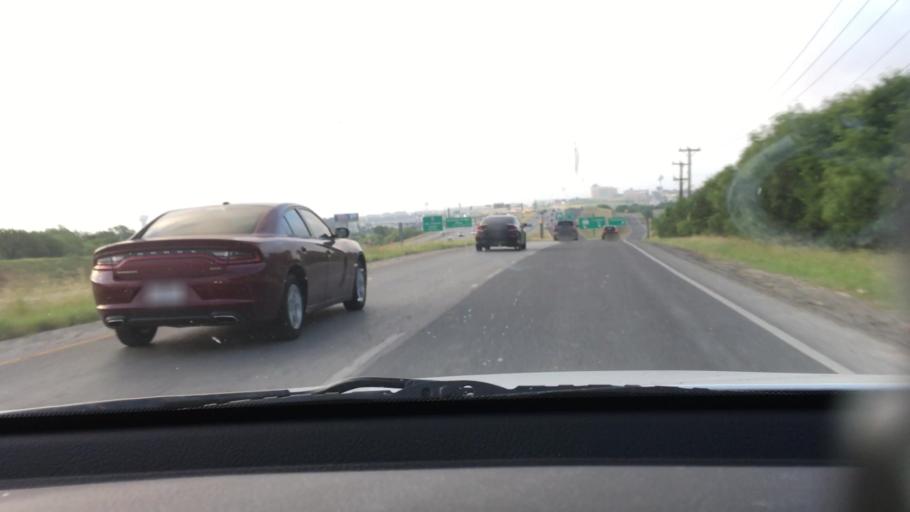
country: US
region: Texas
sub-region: Bexar County
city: Live Oak
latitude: 29.5866
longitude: -98.3490
